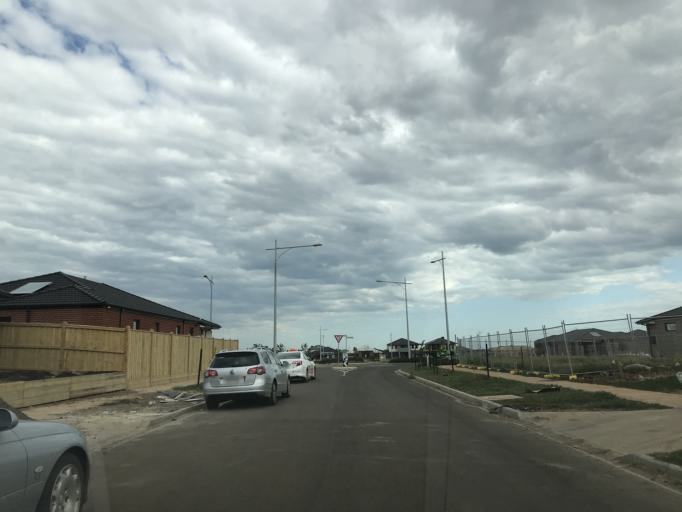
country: AU
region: Victoria
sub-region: Wyndham
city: Truganina
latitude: -37.8251
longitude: 144.7267
